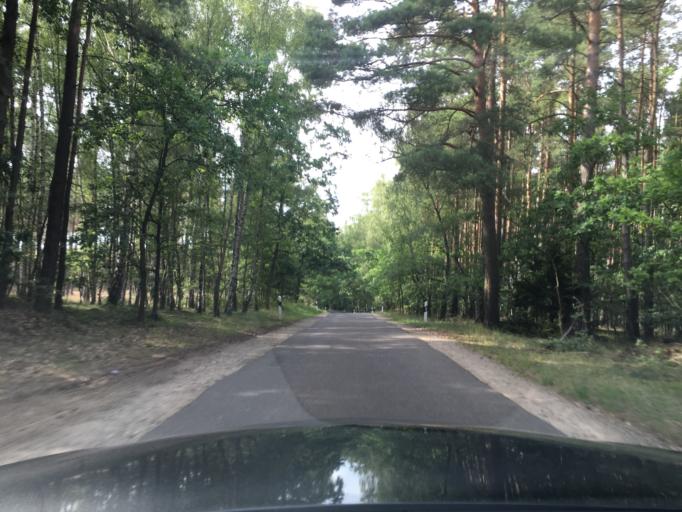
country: DE
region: Mecklenburg-Vorpommern
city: Mollenhagen
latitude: 53.4476
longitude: 12.8259
